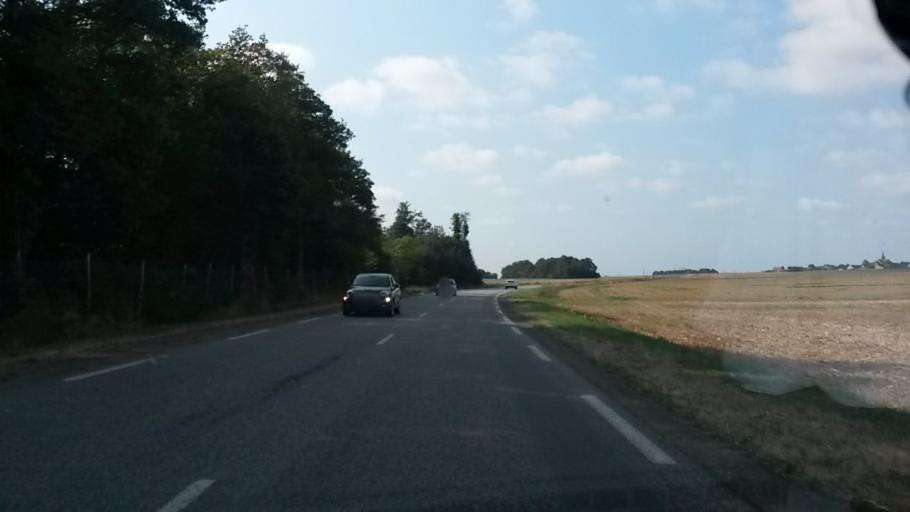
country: FR
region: Haute-Normandie
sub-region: Departement de l'Eure
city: Tillieres-sur-Avre
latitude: 48.8144
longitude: 1.0055
